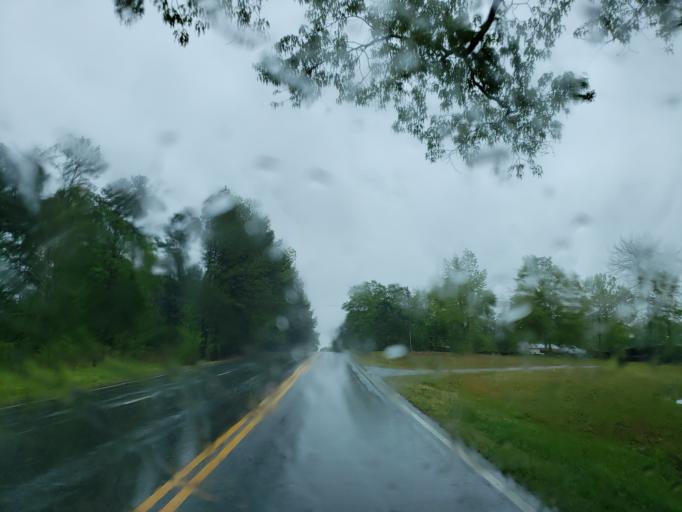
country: US
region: Georgia
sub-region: Carroll County
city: Temple
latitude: 33.7374
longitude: -84.9818
